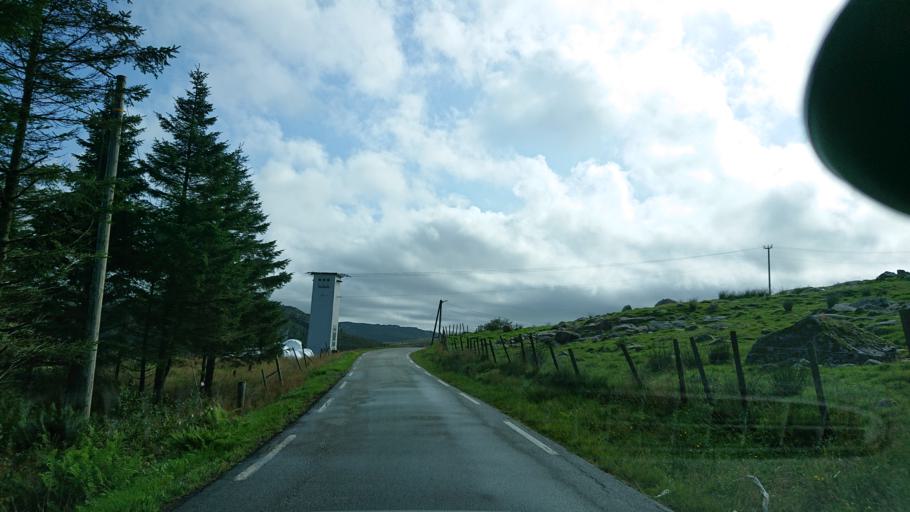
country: NO
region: Rogaland
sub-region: Gjesdal
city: Algard
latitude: 58.6985
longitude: 5.8890
